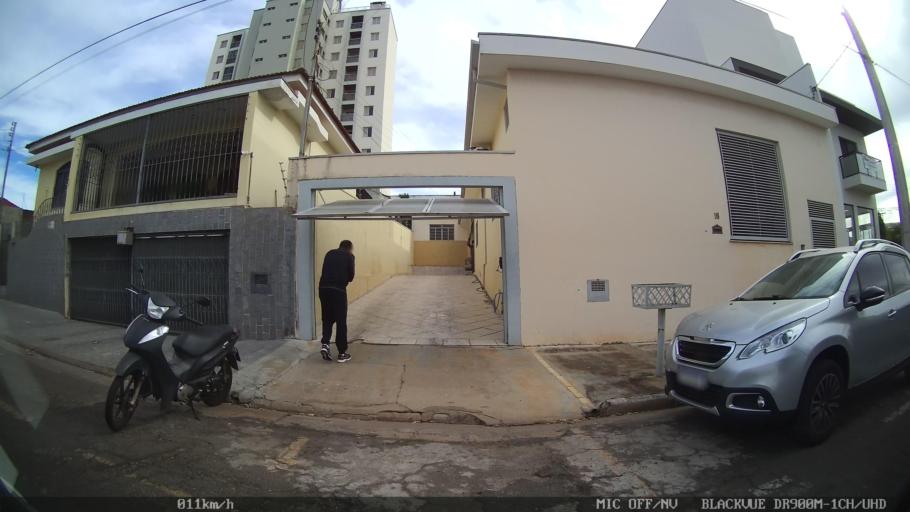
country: BR
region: Sao Paulo
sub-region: Catanduva
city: Catanduva
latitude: -21.1437
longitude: -48.9789
